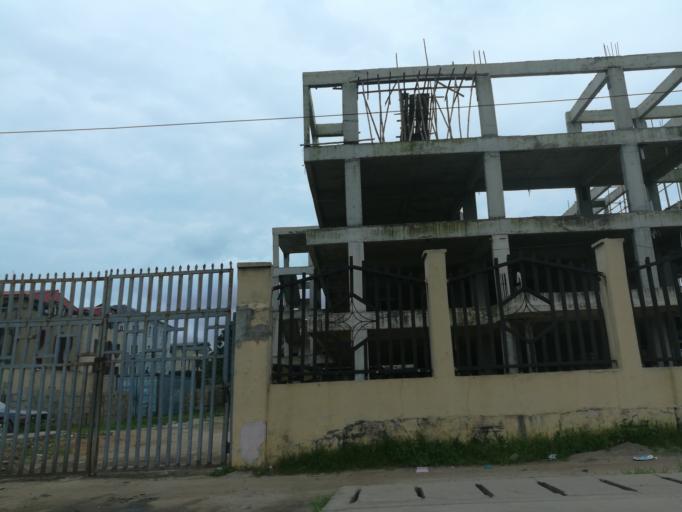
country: NG
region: Lagos
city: Ebute Metta
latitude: 6.4849
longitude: 3.3819
